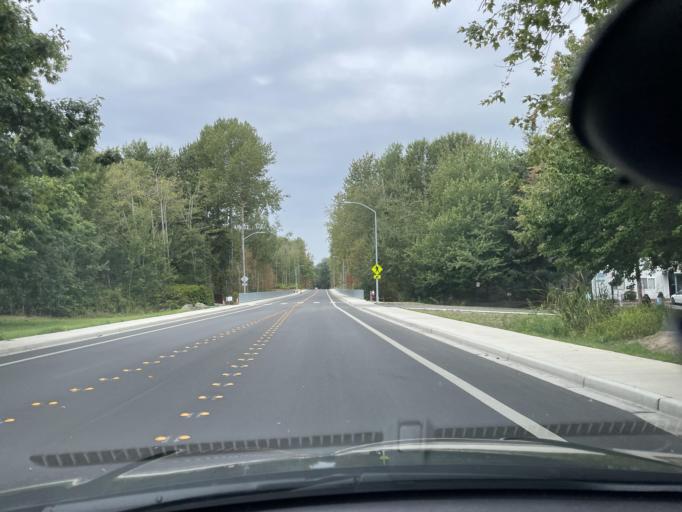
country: US
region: Washington
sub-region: Whatcom County
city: Bellingham
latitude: 48.8043
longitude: -122.5016
